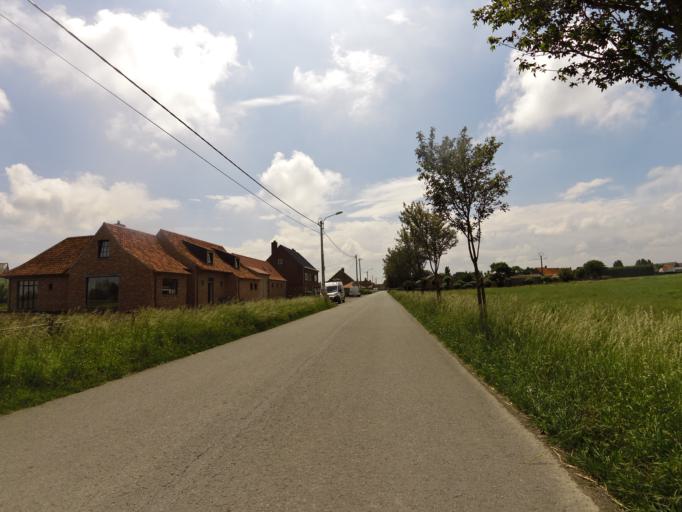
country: BE
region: Flanders
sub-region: Provincie West-Vlaanderen
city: Middelkerke
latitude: 51.1287
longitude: 2.8179
